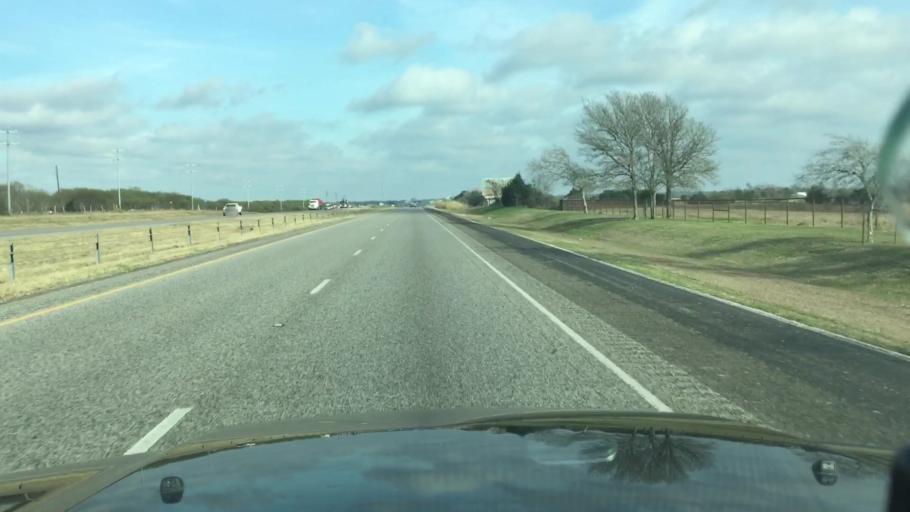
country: US
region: Texas
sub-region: Washington County
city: Brenham
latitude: 30.1378
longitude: -96.3228
